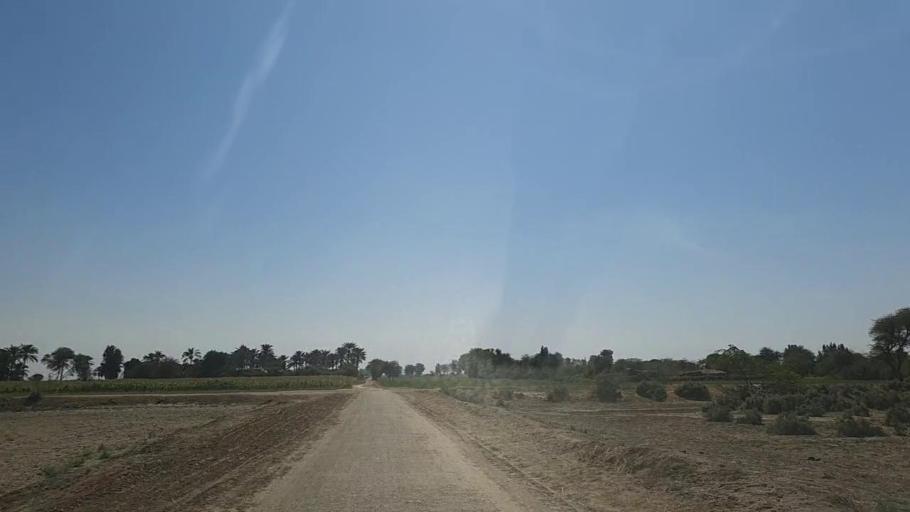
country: PK
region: Sindh
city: Samaro
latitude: 25.2932
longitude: 69.5027
